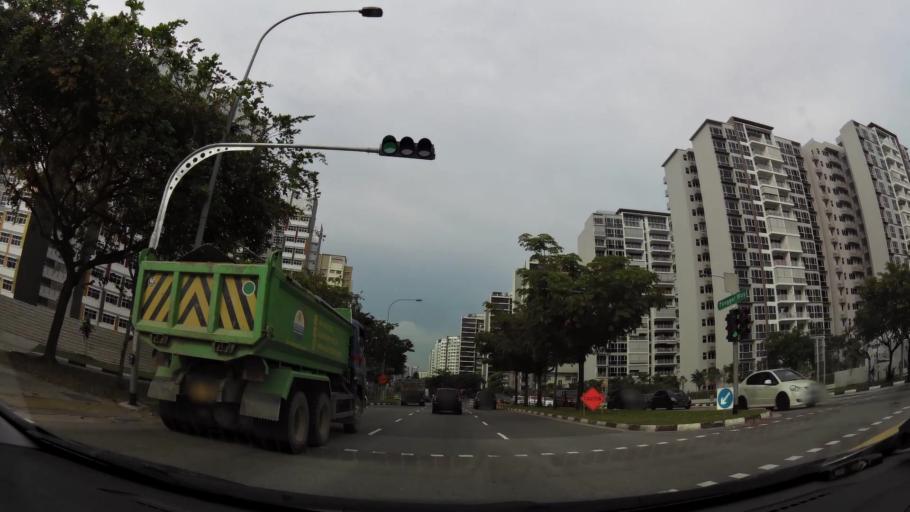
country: MY
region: Johor
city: Kampung Pasir Gudang Baru
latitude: 1.4005
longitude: 103.8961
